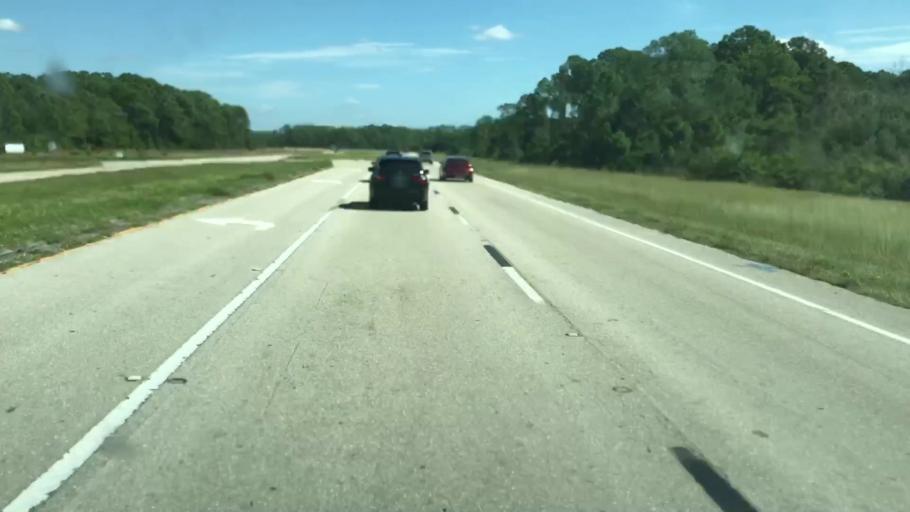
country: US
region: Florida
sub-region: Lee County
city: Gateway
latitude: 26.5592
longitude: -81.7438
